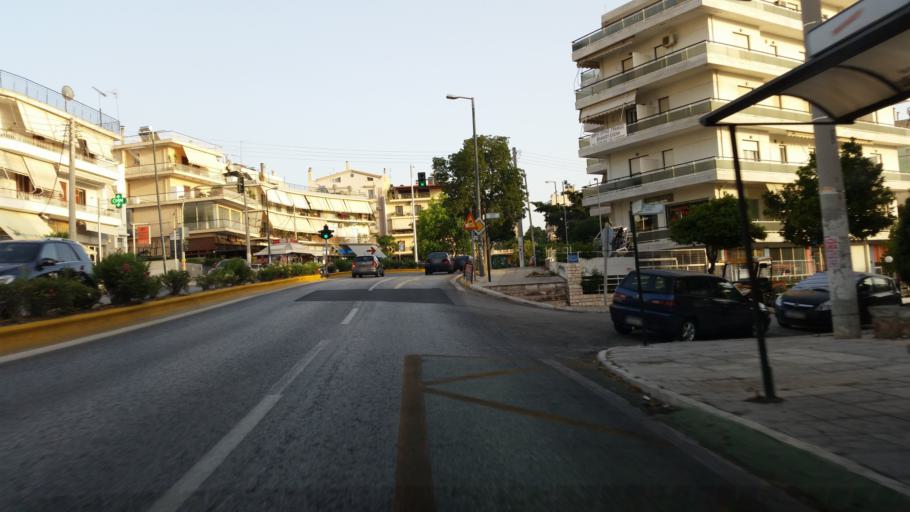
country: GR
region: Attica
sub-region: Nomarchia Athinas
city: Ilioupoli
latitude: 37.9298
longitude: 23.7592
